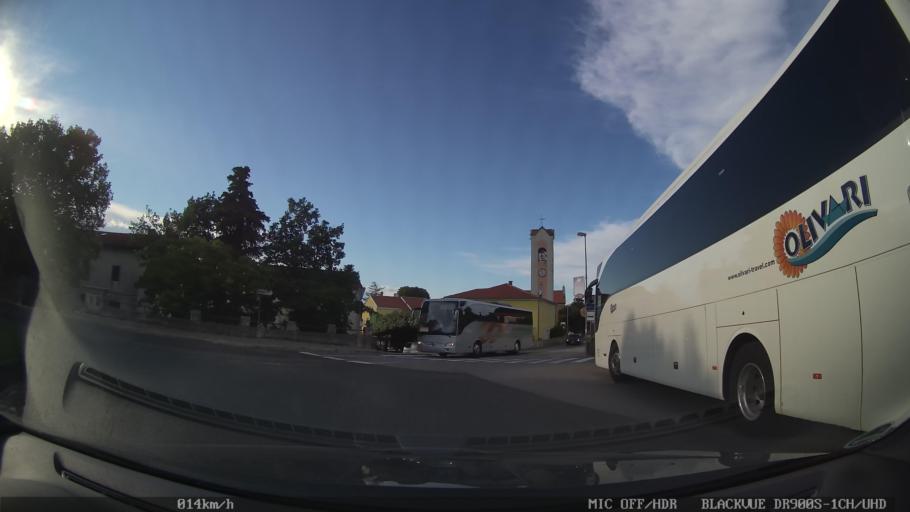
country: HR
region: Primorsko-Goranska
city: Njivice
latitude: 45.1171
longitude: 14.5269
